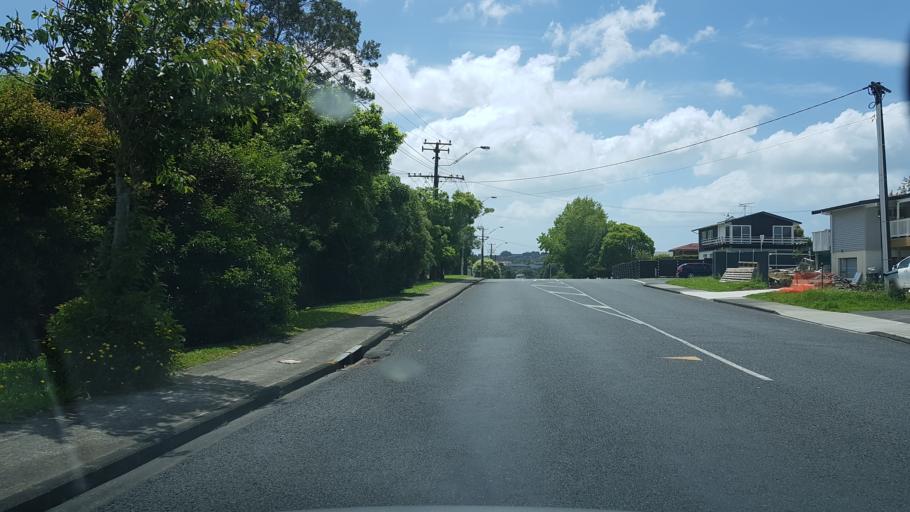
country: NZ
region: Auckland
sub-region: Auckland
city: North Shore
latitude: -36.7875
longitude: 174.7007
